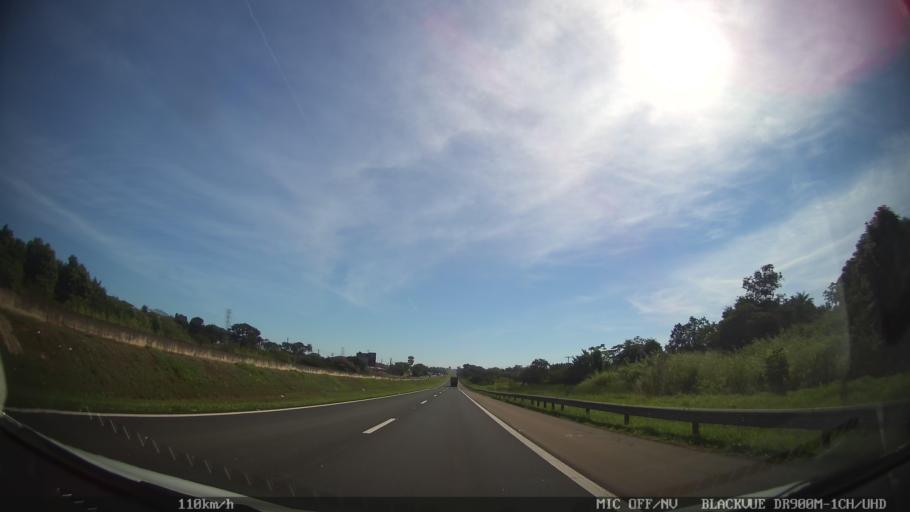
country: BR
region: Sao Paulo
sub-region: Pirassununga
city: Pirassununga
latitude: -22.0057
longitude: -47.4431
